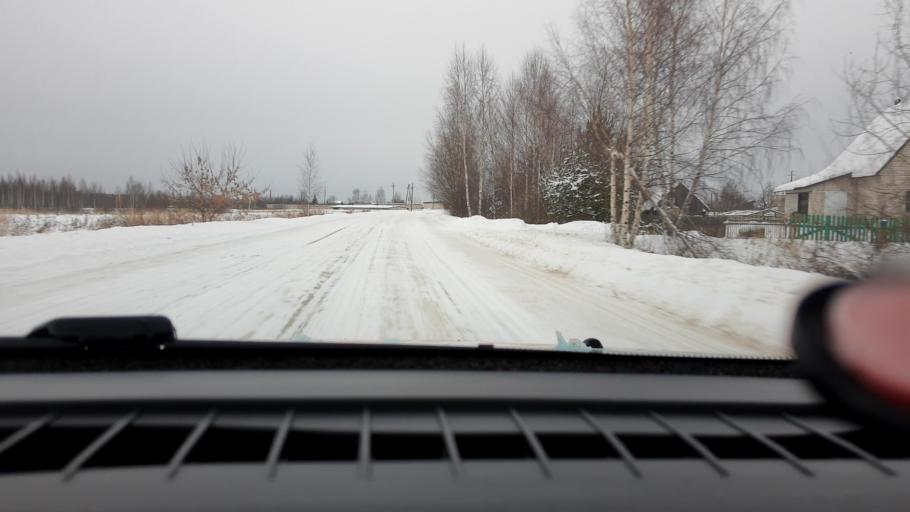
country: RU
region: Nizjnij Novgorod
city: Sitniki
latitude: 56.5226
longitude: 44.0411
